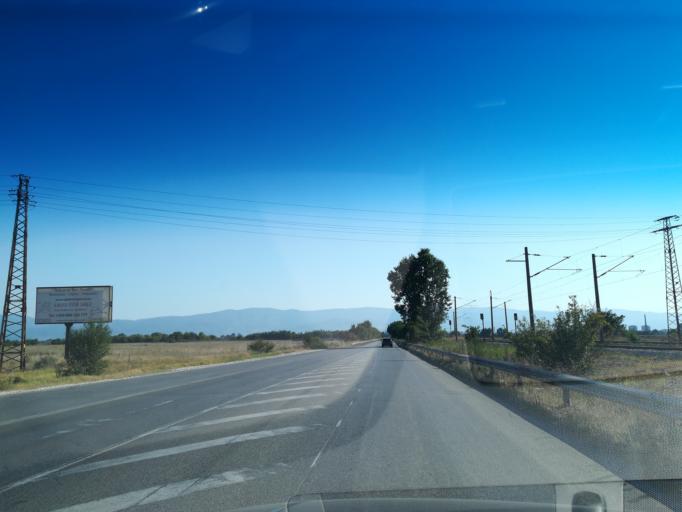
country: BG
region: Plovdiv
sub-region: Obshtina Plovdiv
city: Plovdiv
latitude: 42.1722
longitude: 24.8195
